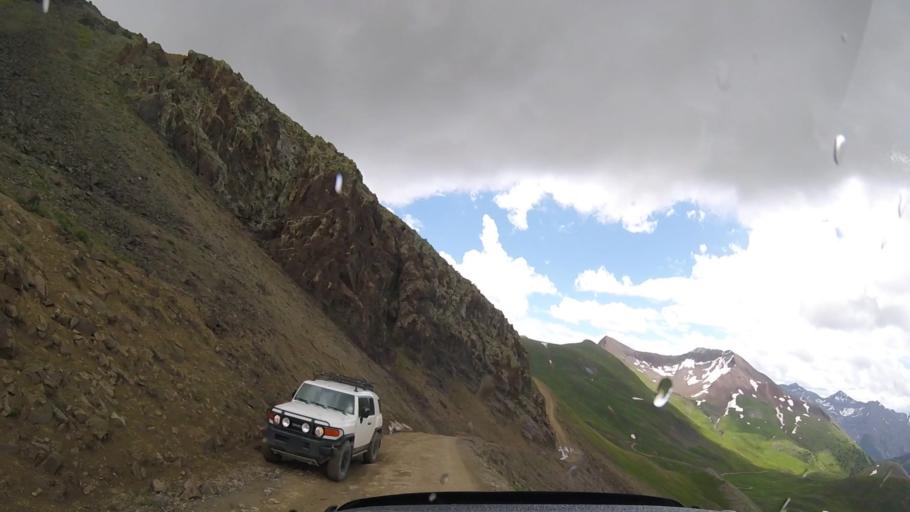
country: US
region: Colorado
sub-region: Ouray County
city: Ouray
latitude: 37.9665
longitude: -107.5857
